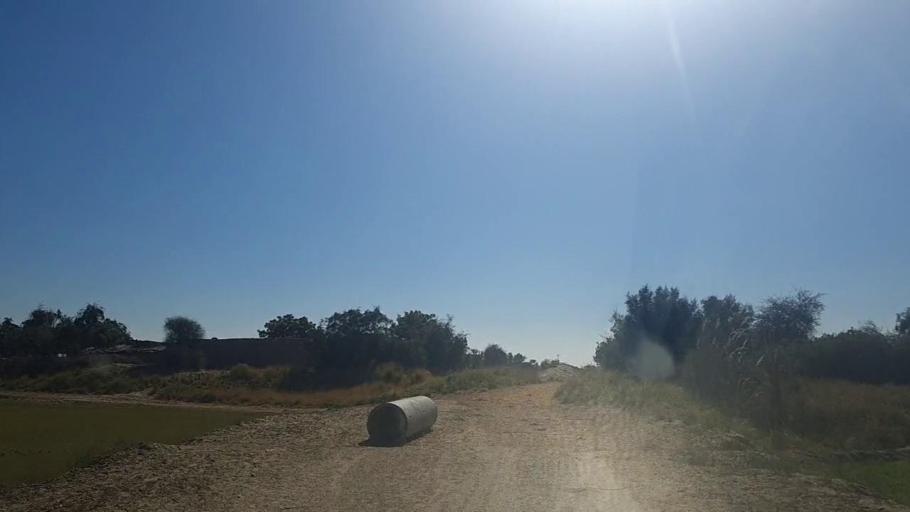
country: PK
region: Sindh
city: Sanghar
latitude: 26.1929
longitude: 68.9106
